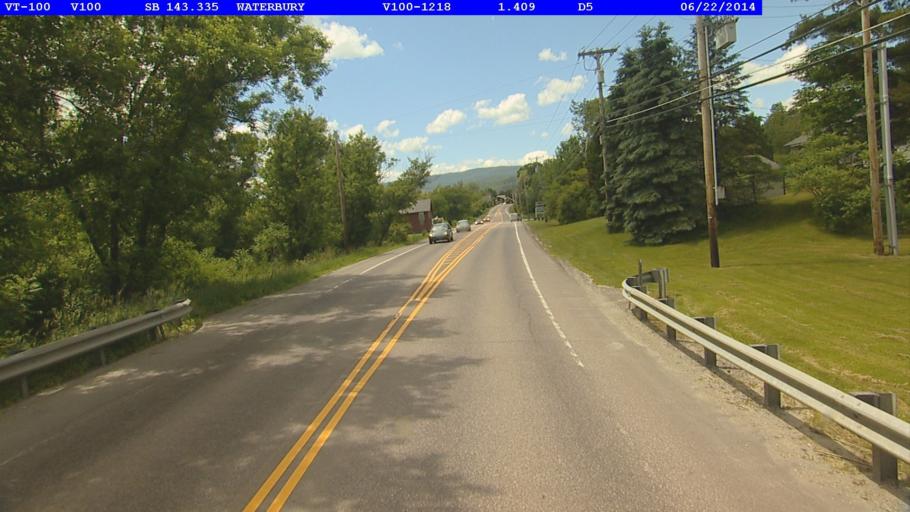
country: US
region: Vermont
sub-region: Washington County
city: Waterbury
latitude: 44.3527
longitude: -72.7380
